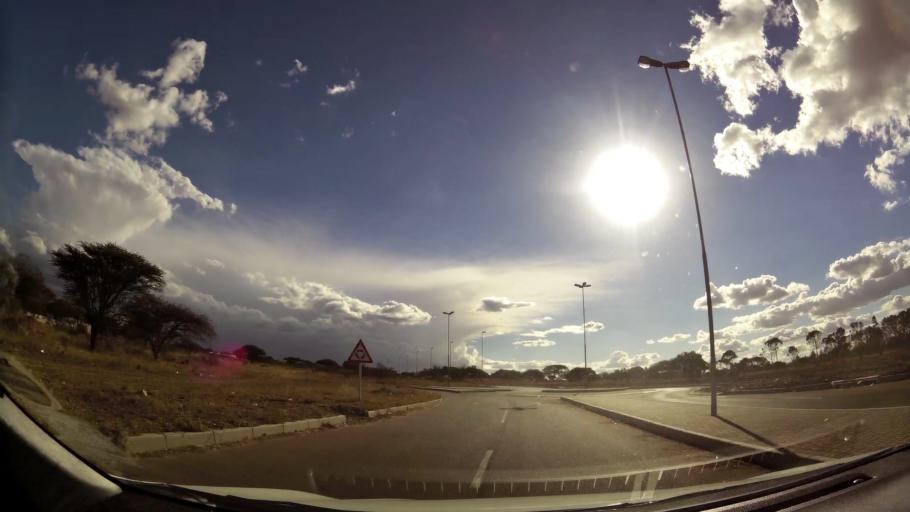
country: ZA
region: Limpopo
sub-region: Capricorn District Municipality
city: Polokwane
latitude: -23.9355
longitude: 29.4480
